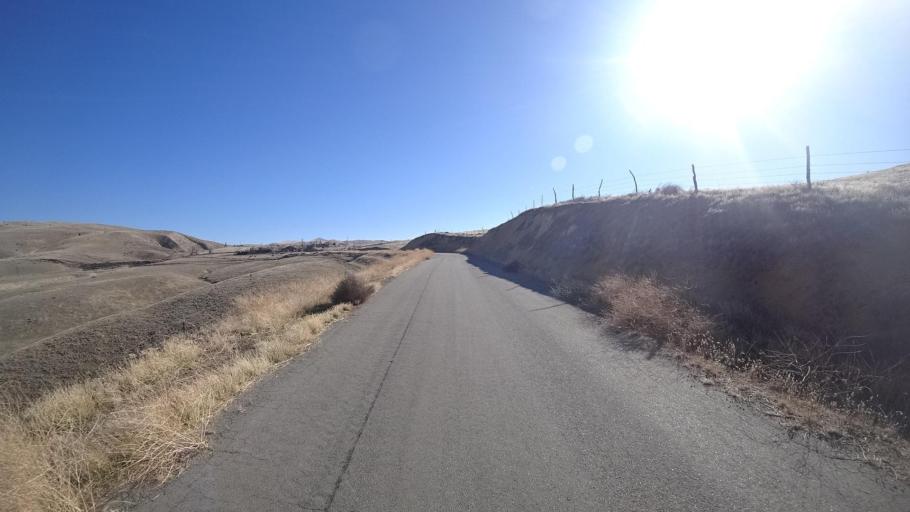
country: US
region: California
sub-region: Kern County
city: Maricopa
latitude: 34.9657
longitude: -119.4486
